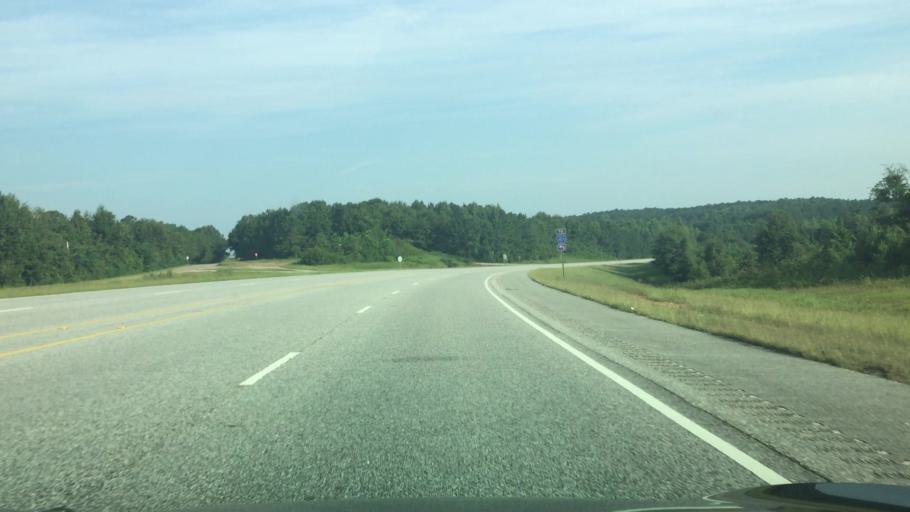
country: US
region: Alabama
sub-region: Butler County
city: Georgiana
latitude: 31.5039
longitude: -86.7000
